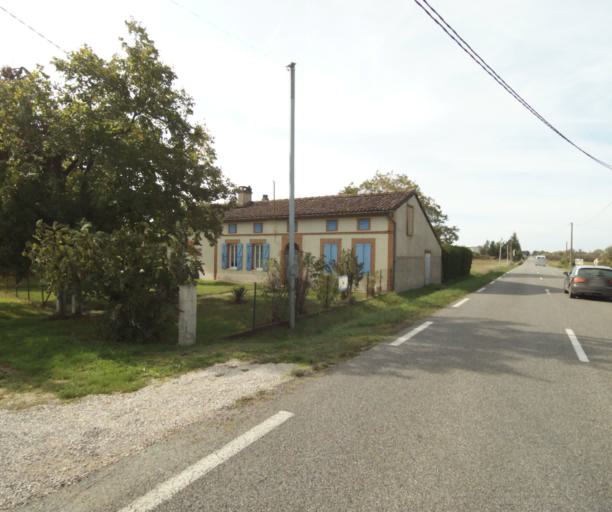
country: FR
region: Midi-Pyrenees
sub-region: Departement du Tarn-et-Garonne
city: Labastide-Saint-Pierre
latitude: 43.9118
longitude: 1.3858
